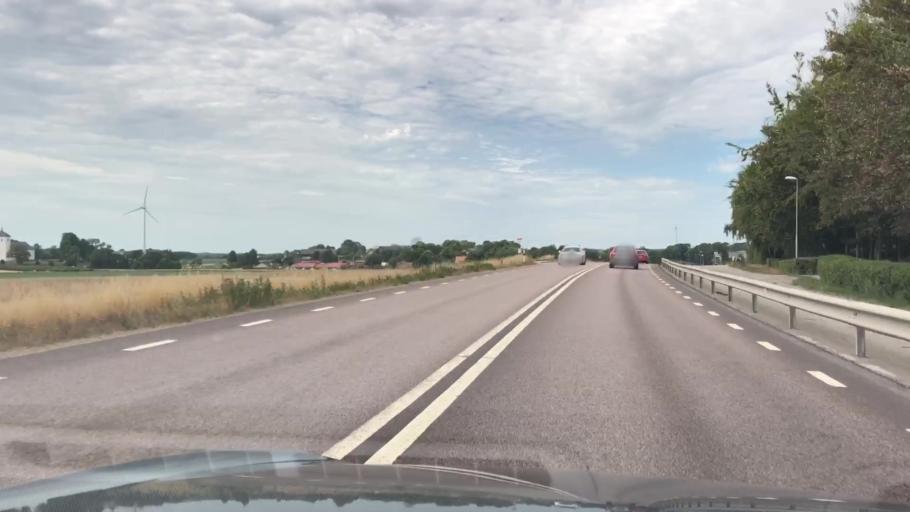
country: SE
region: Blekinge
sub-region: Karlskrona Kommun
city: Jaemjoe
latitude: 56.1837
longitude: 15.7787
